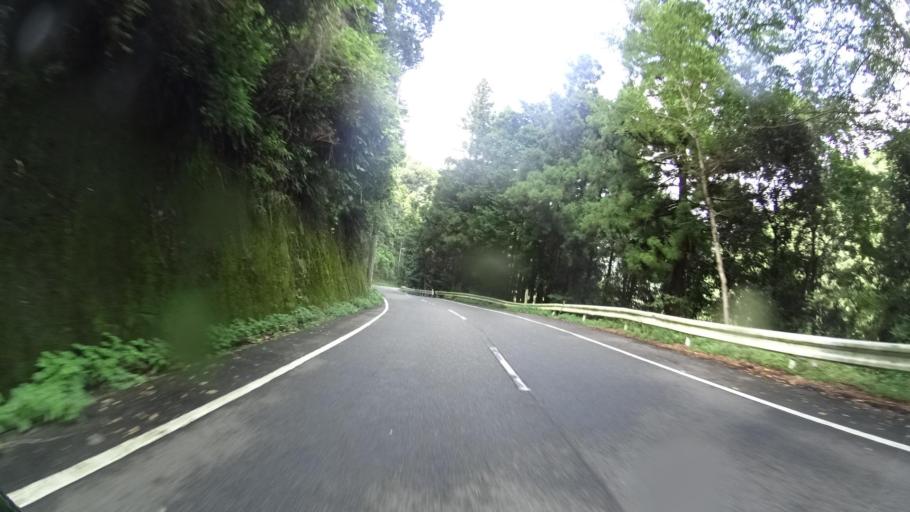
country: JP
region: Mie
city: Ueno-ebisumachi
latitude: 34.7678
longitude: 135.9991
